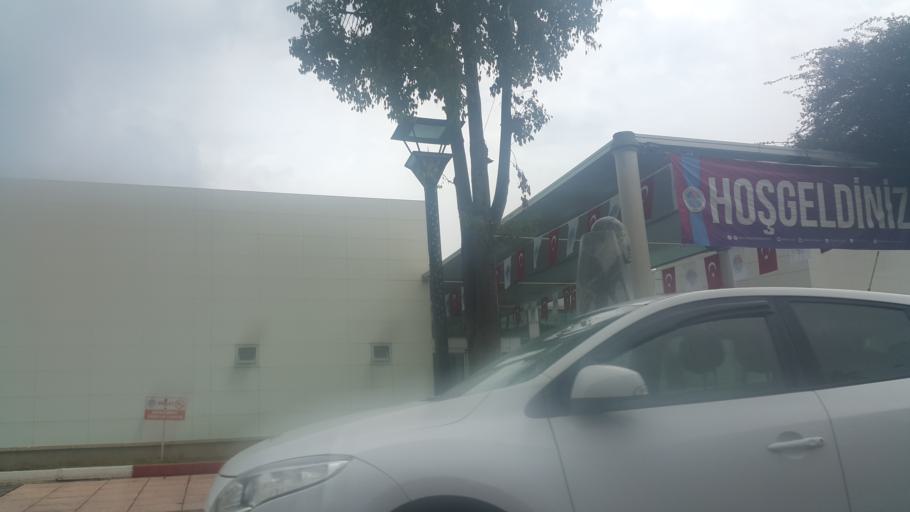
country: TR
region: Mersin
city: Mercin
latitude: 36.7995
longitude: 34.6339
